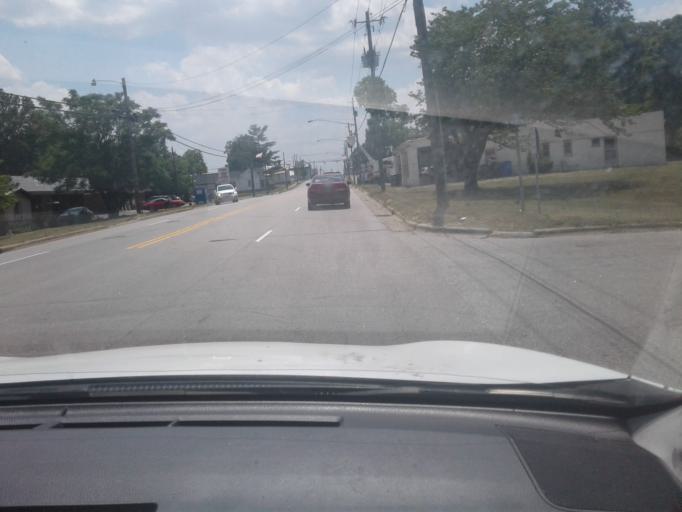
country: US
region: North Carolina
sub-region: Johnston County
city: Benson
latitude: 35.3846
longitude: -78.5468
